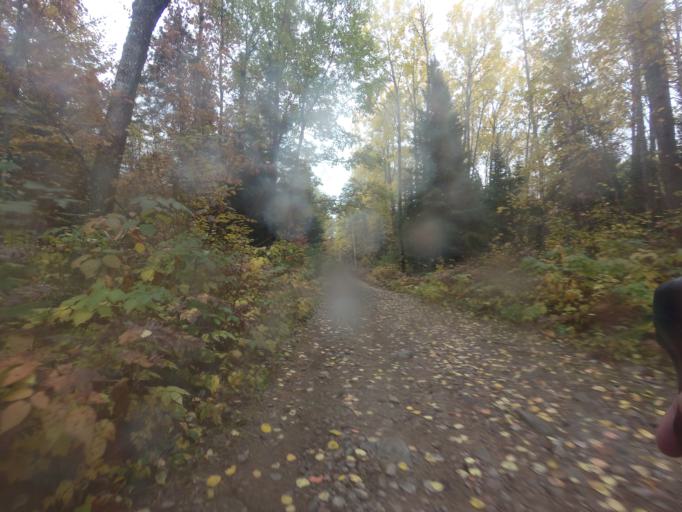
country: CA
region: Ontario
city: Petawawa
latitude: 45.7882
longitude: -77.3819
